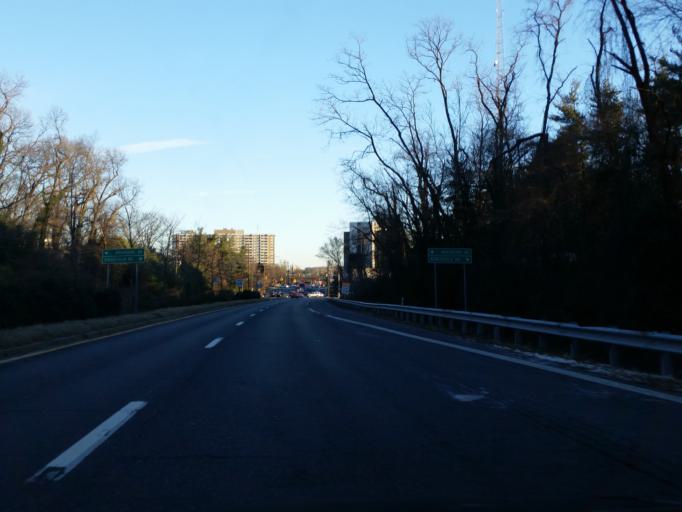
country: US
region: Maryland
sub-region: Montgomery County
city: Somerset
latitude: 38.9679
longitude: -77.1083
